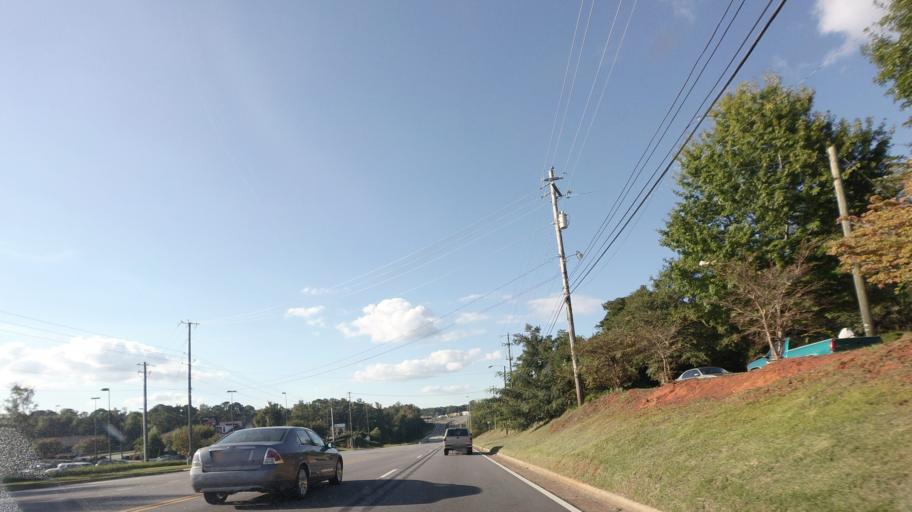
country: US
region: Georgia
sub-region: Upson County
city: Hannahs Mill
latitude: 32.9140
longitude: -84.3315
